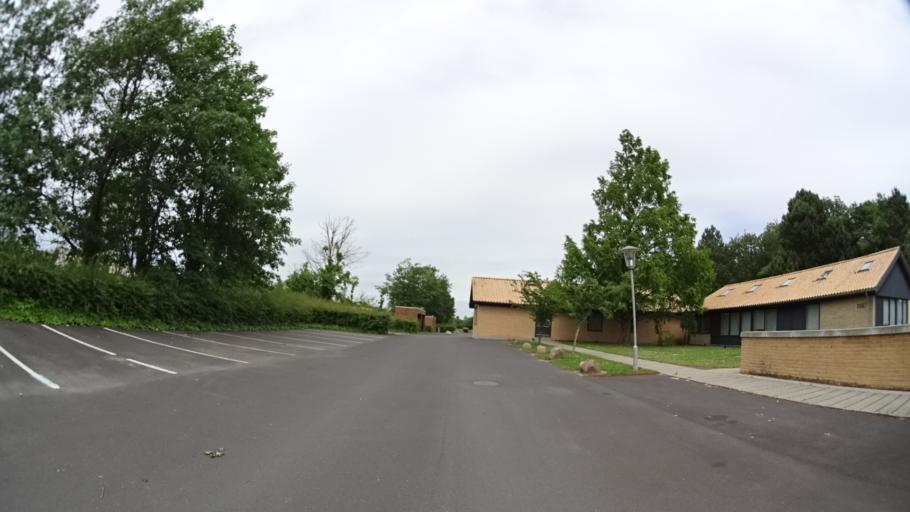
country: DK
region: Central Jutland
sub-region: Arhus Kommune
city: Stavtrup
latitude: 56.1199
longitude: 10.1337
